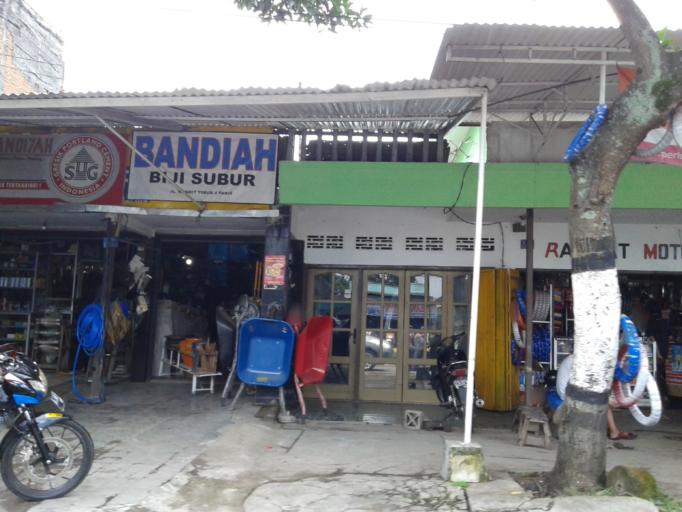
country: ID
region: East Java
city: Malang
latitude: -7.9514
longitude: 112.6770
